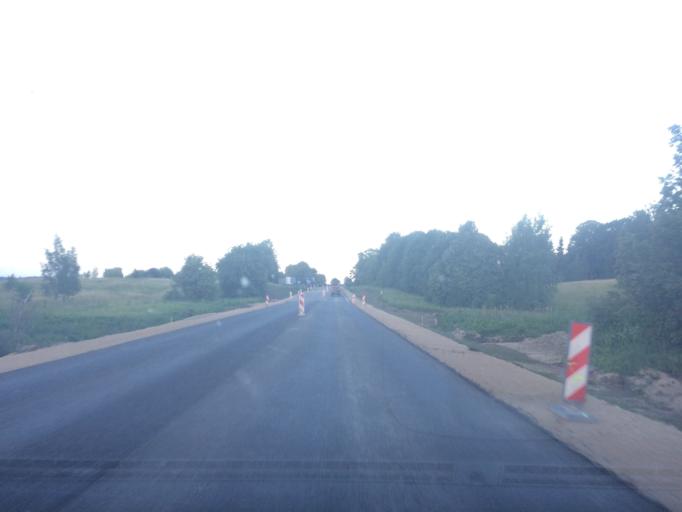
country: LT
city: Zarasai
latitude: 55.7486
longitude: 26.3159
